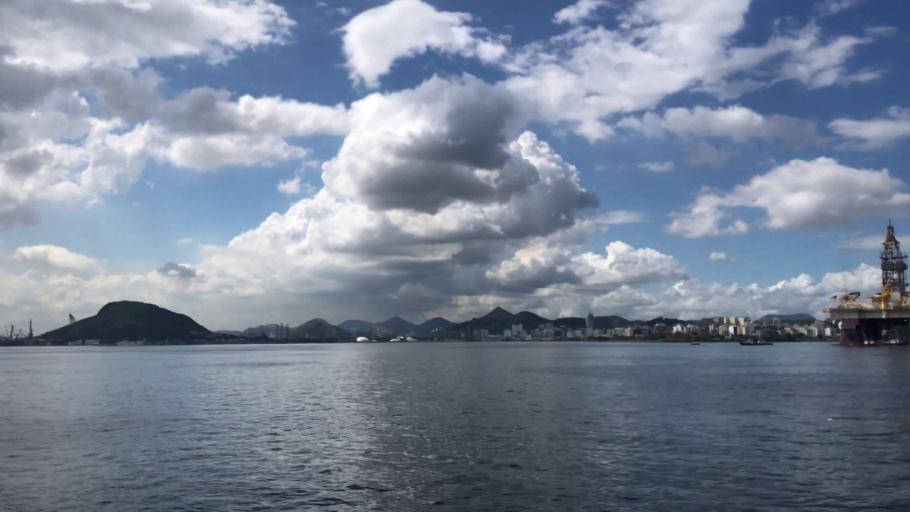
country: BR
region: Rio de Janeiro
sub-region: Niteroi
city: Niteroi
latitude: -22.8964
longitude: -43.1472
